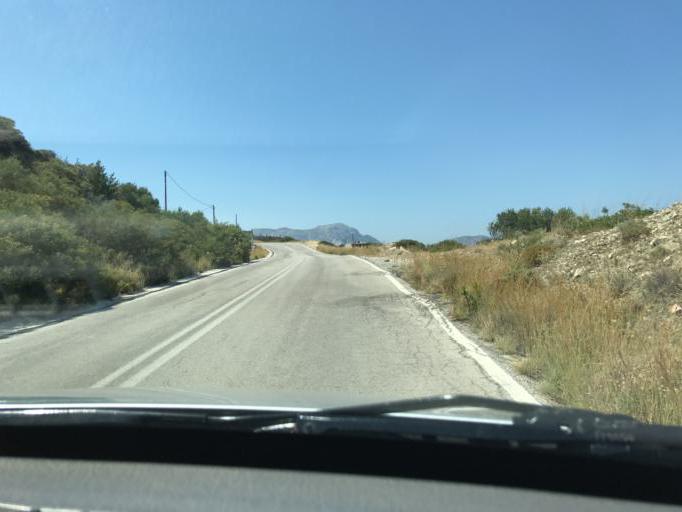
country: GR
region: South Aegean
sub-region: Nomos Dodekanisou
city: Karpathos
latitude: 35.4840
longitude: 27.1831
